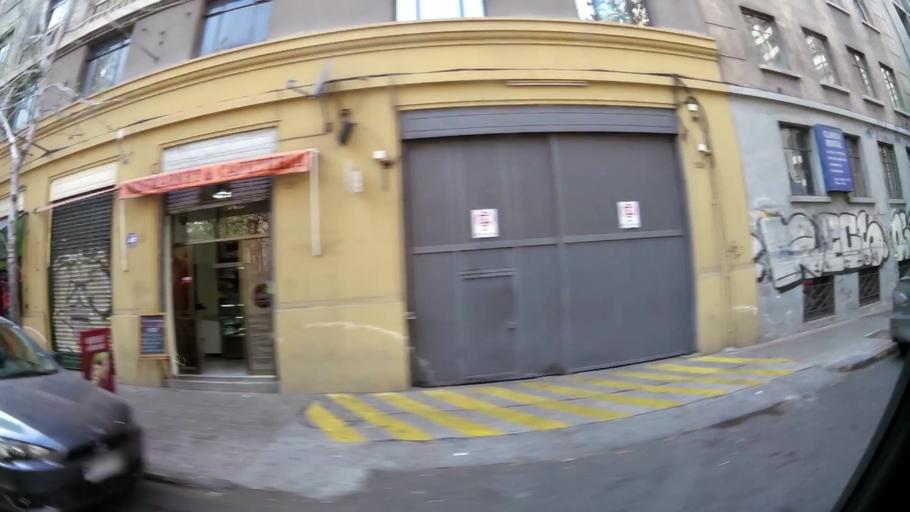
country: CL
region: Santiago Metropolitan
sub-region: Provincia de Santiago
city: Santiago
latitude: -33.4467
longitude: -70.6537
